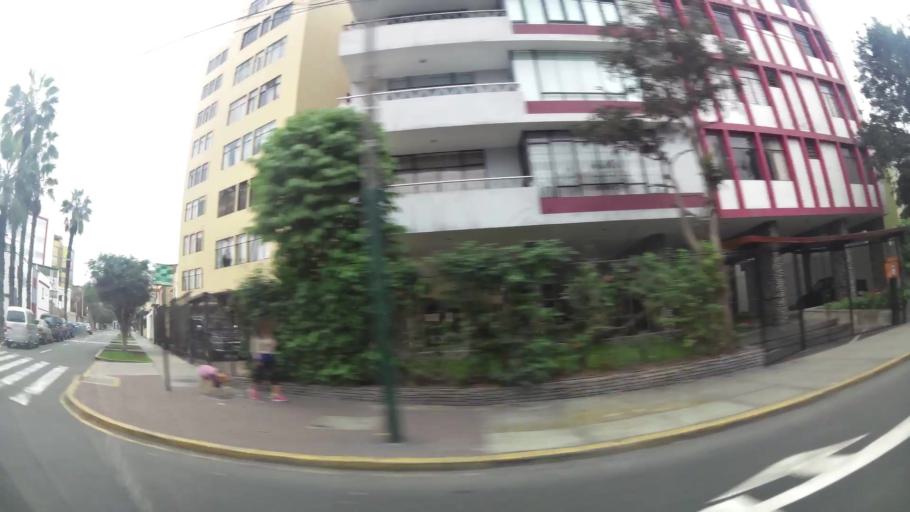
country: PE
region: Lima
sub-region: Lima
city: San Isidro
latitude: -12.1019
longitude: -77.0318
